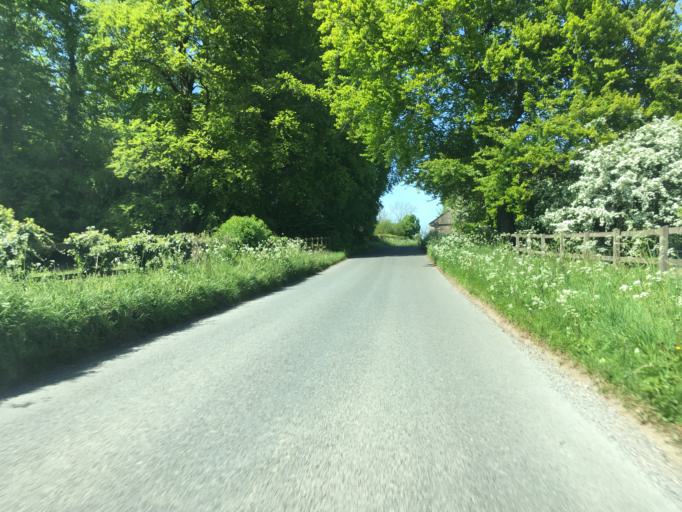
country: GB
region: England
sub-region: Gloucestershire
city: Coates
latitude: 51.7250
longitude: -2.0776
